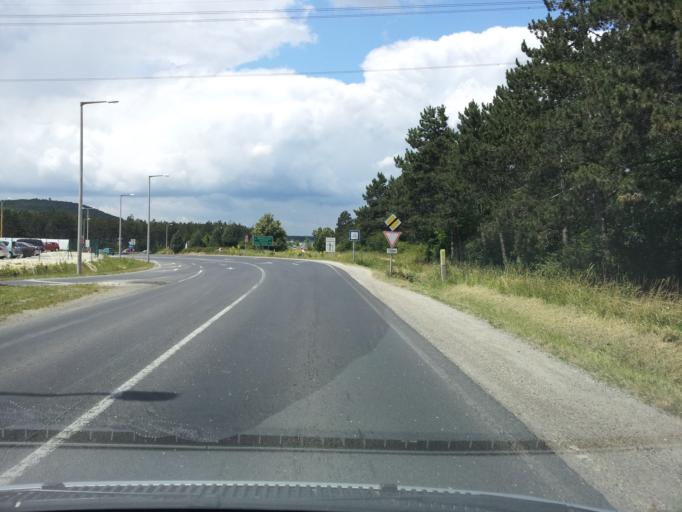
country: HU
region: Veszprem
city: Veszprem
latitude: 47.1080
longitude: 17.8679
